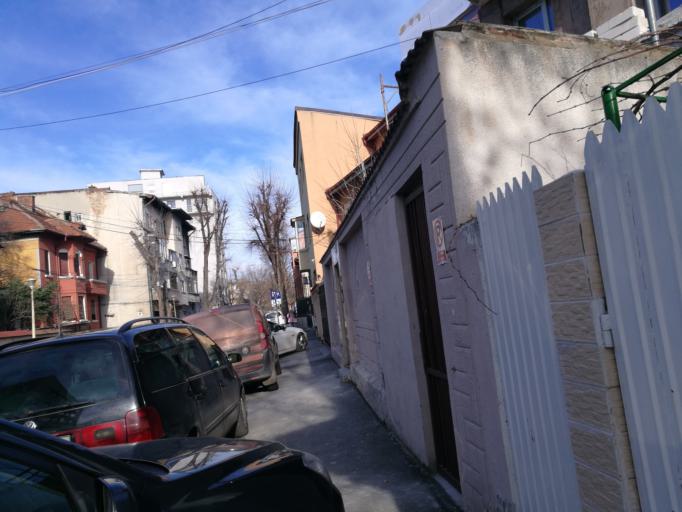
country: RO
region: Bucuresti
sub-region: Municipiul Bucuresti
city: Bucharest
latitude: 44.4351
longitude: 26.1328
